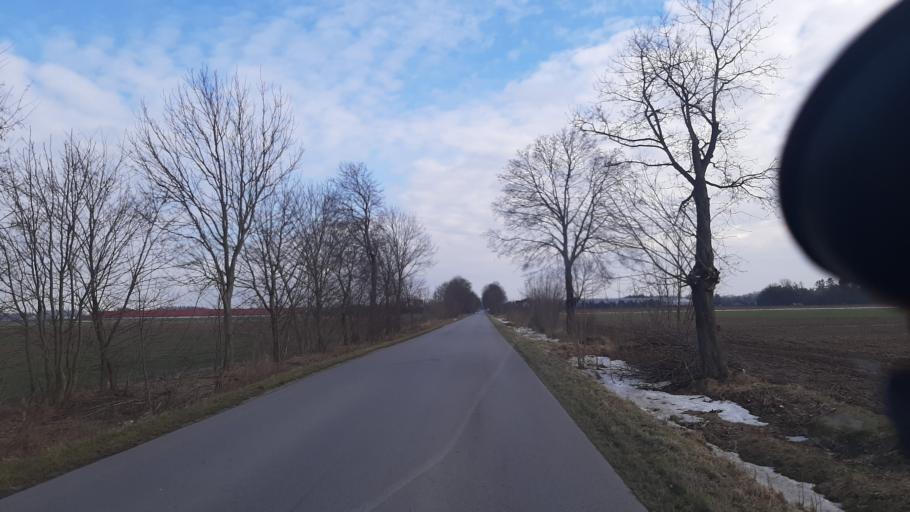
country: PL
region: Lublin Voivodeship
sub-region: Powiat lubartowski
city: Ostrow Lubelski
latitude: 51.4814
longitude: 22.9018
